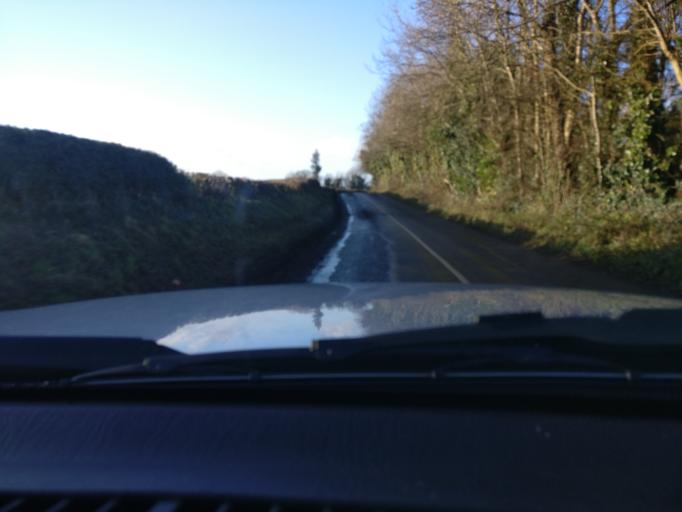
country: IE
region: Leinster
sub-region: An Mhi
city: Athboy
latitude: 53.6955
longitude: -7.0036
